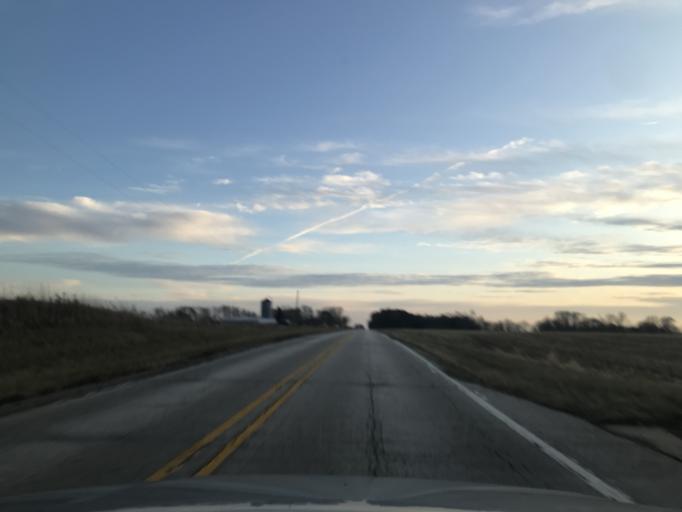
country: US
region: Illinois
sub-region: Henderson County
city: Oquawka
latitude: 40.9580
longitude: -90.8639
